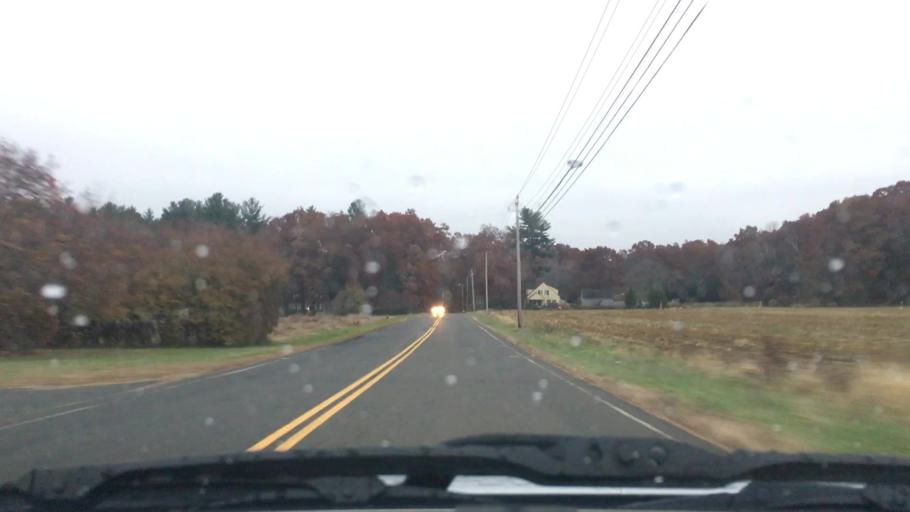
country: US
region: Massachusetts
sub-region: Hampden County
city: Westfield
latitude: 42.1062
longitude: -72.7820
